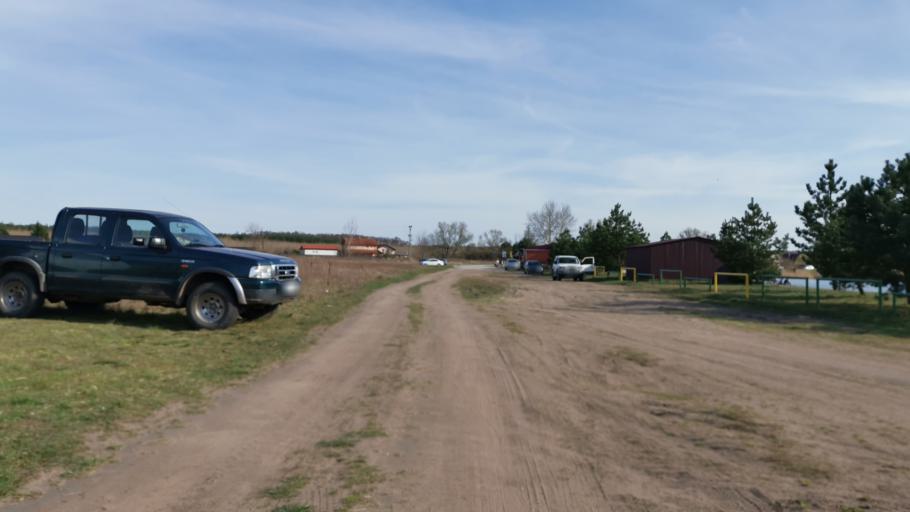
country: CZ
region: South Moravian
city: Tvrdonice
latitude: 48.7307
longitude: 17.0375
